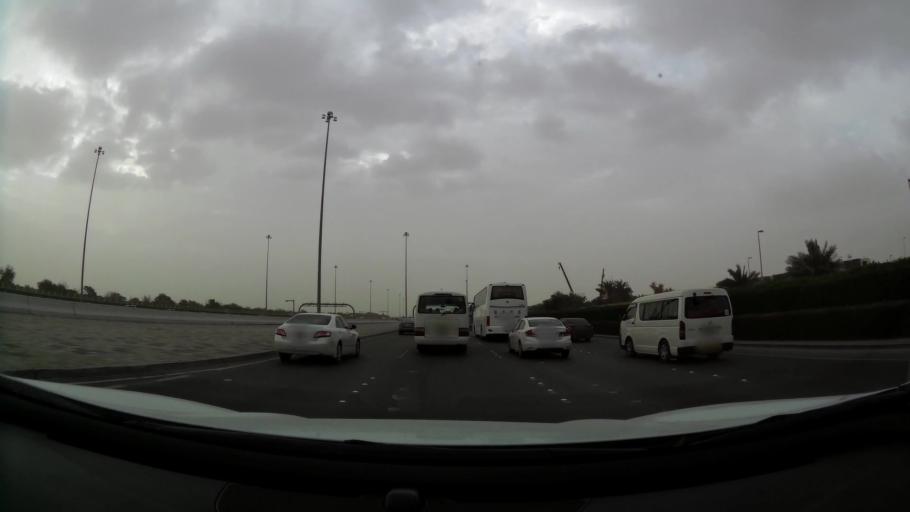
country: AE
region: Abu Dhabi
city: Abu Dhabi
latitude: 24.4789
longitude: 54.3874
